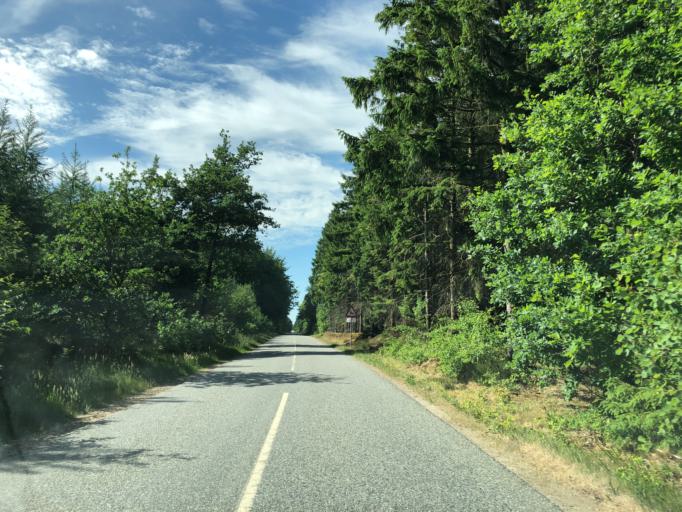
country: DK
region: Central Jutland
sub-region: Herning Kommune
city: Lind
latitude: 56.0201
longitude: 8.9705
